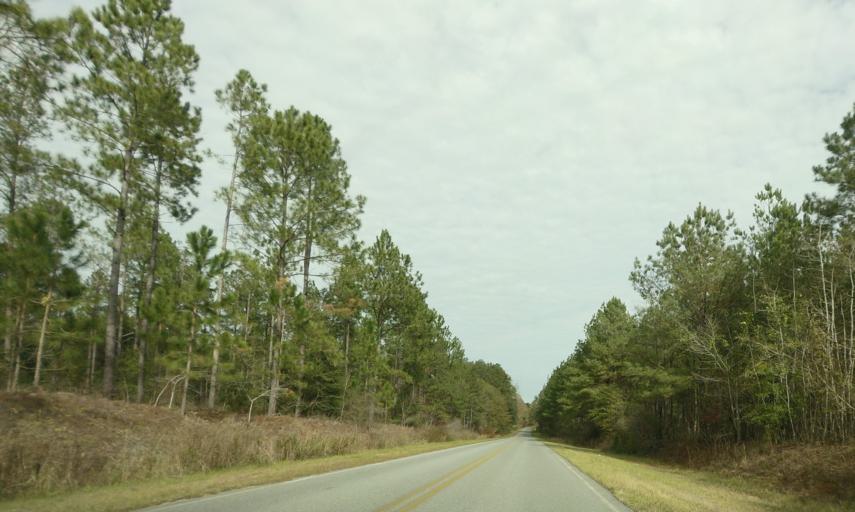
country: US
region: Georgia
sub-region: Dodge County
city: Chester
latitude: 32.4851
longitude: -83.0913
